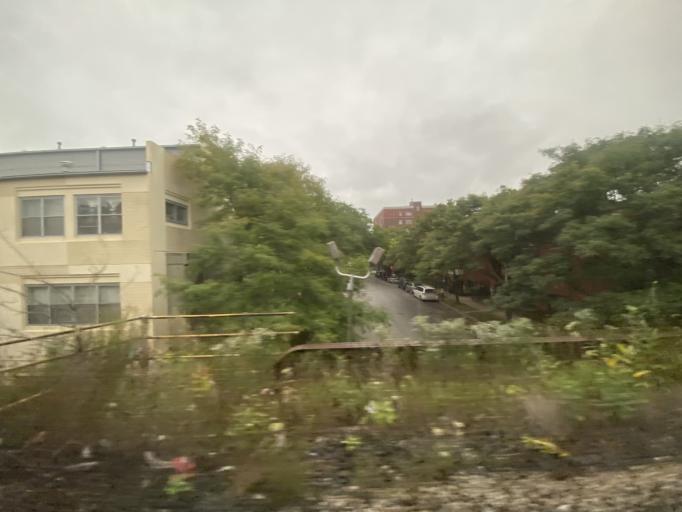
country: US
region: Illinois
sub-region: Cook County
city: Chicago
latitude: 41.8510
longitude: -87.6367
